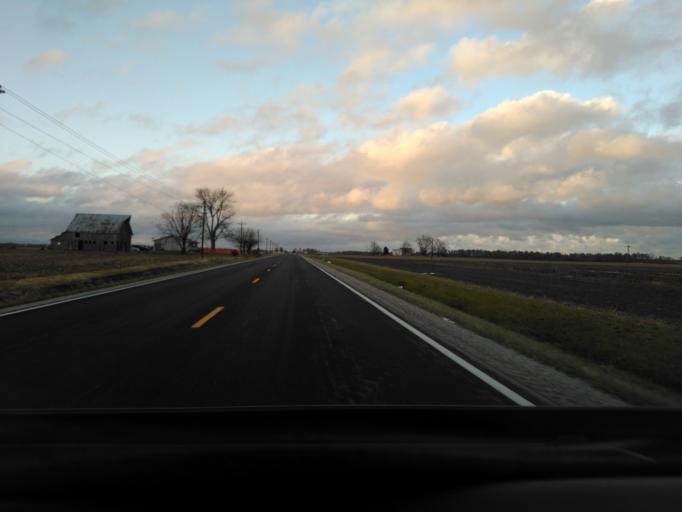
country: US
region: Illinois
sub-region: Effingham County
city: Altamont
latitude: 38.9988
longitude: -88.7486
